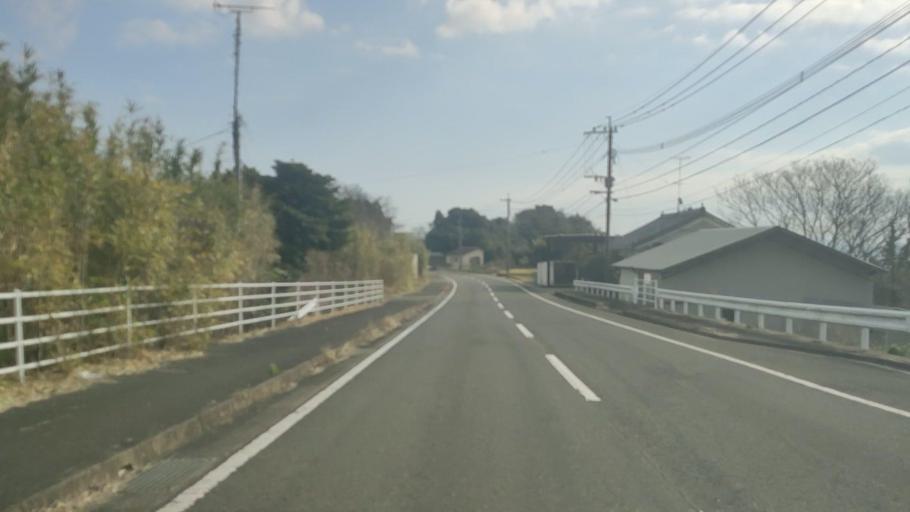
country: JP
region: Nagasaki
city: Shimabara
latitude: 32.6807
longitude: 130.2765
